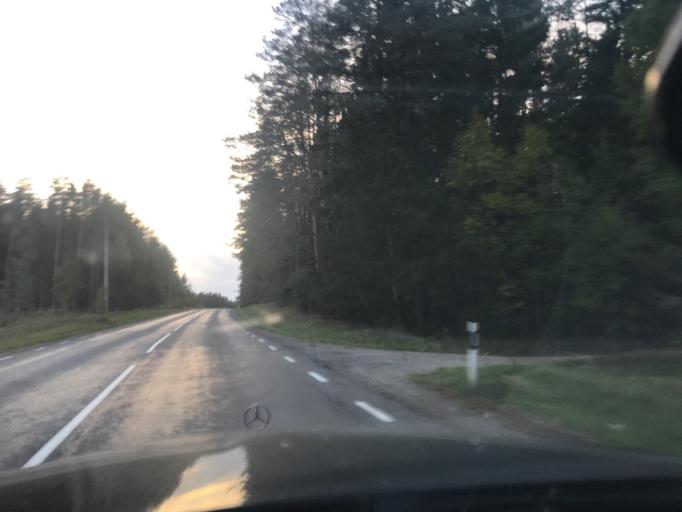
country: EE
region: Valgamaa
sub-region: Torva linn
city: Torva
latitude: 58.0094
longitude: 26.1534
